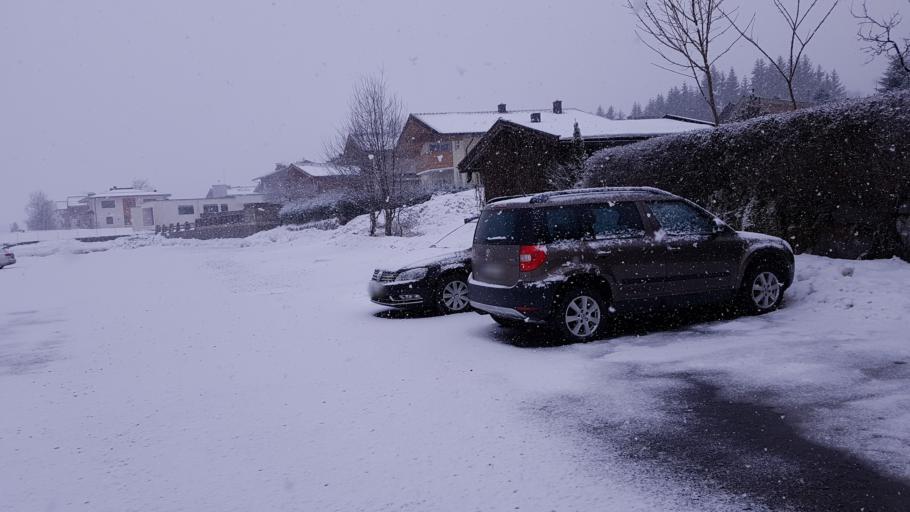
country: AT
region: Salzburg
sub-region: Politischer Bezirk Zell am See
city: Neukirchen am Grossvenediger
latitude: 47.2532
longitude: 12.2823
